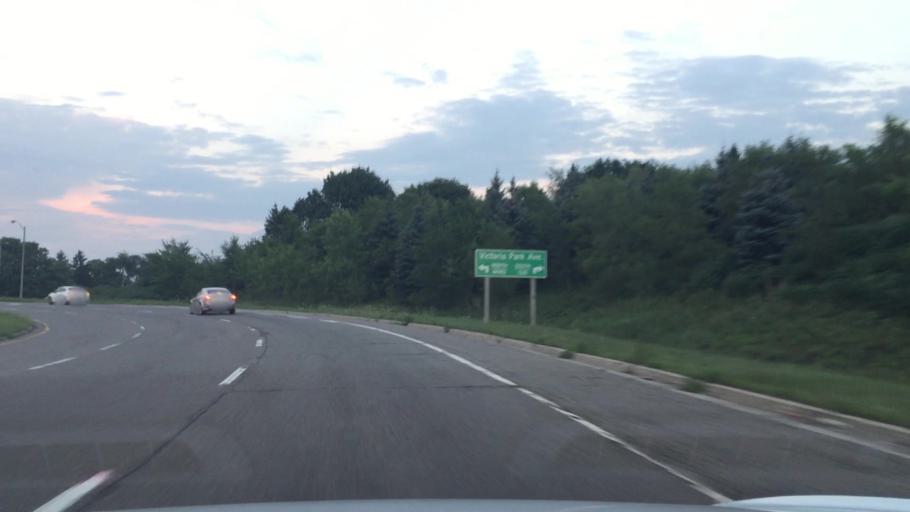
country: CA
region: Ontario
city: Scarborough
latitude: 43.7669
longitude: -79.3208
